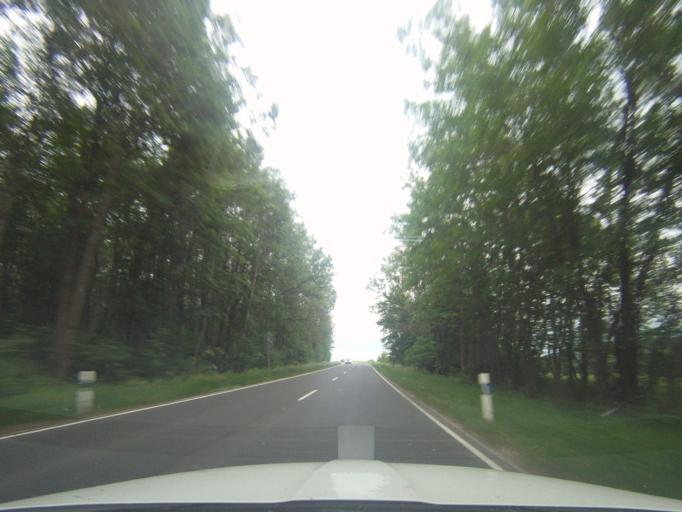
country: DE
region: Thuringia
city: Eisfeld
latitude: 50.4404
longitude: 10.8745
